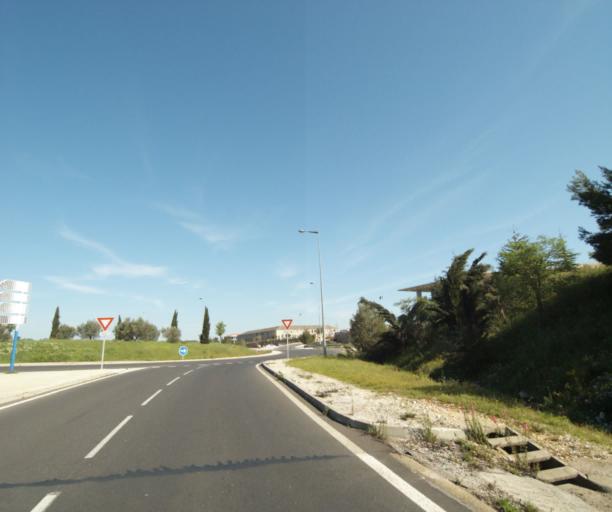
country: FR
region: Languedoc-Roussillon
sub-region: Departement de l'Herault
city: Le Cres
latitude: 43.6481
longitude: 3.9289
